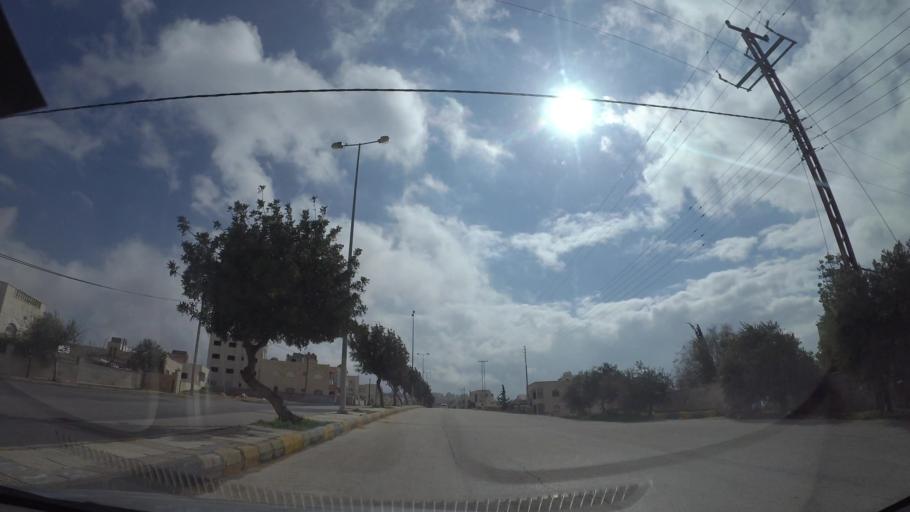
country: JO
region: Amman
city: Al Jubayhah
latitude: 32.0749
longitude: 35.8825
